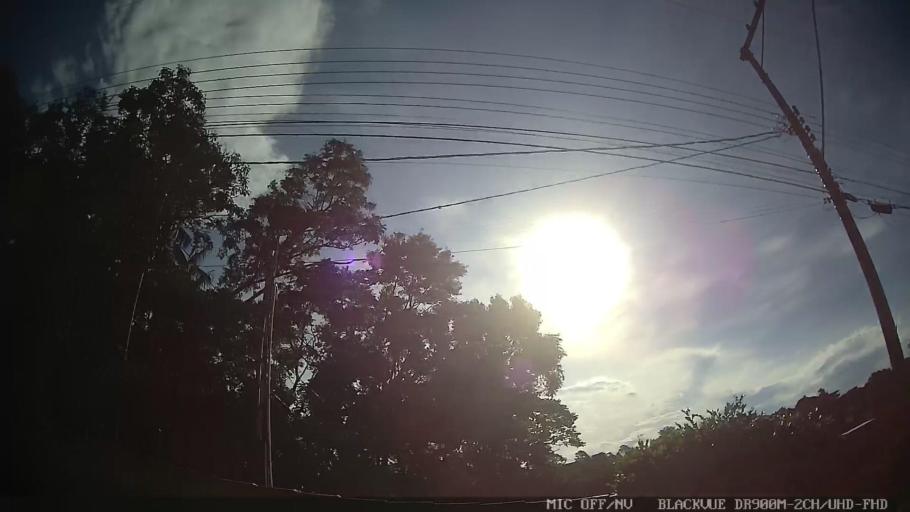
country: BR
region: Sao Paulo
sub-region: Serra Negra
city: Serra Negra
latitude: -22.6384
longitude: -46.6963
